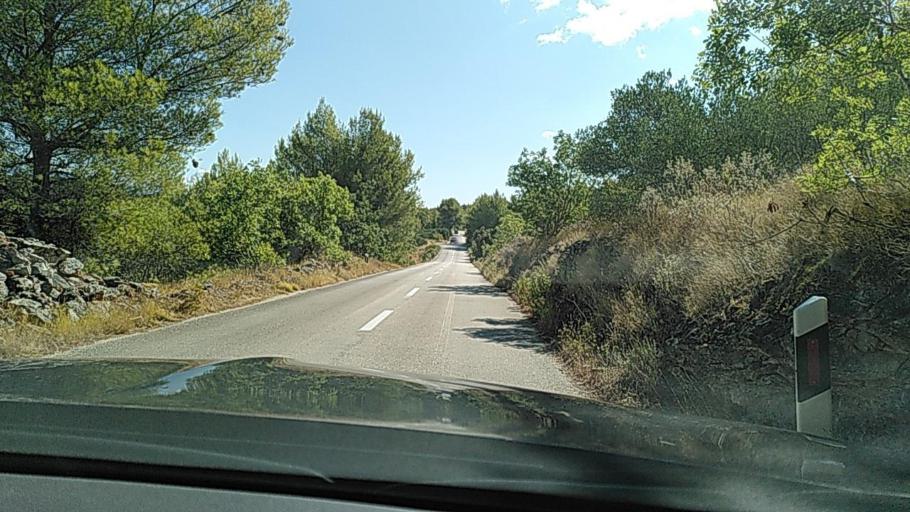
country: HR
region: Splitsko-Dalmatinska
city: Jelsa
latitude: 43.1432
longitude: 16.8170
